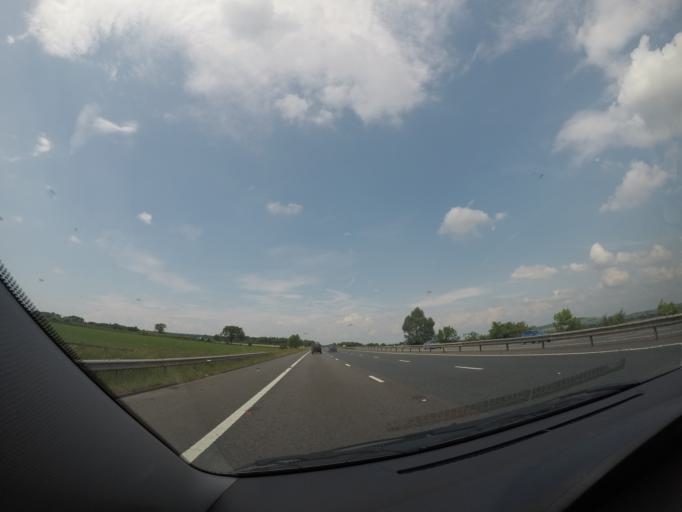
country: GB
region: England
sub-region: Cumbria
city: Scotby
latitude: 54.7777
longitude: -2.8528
